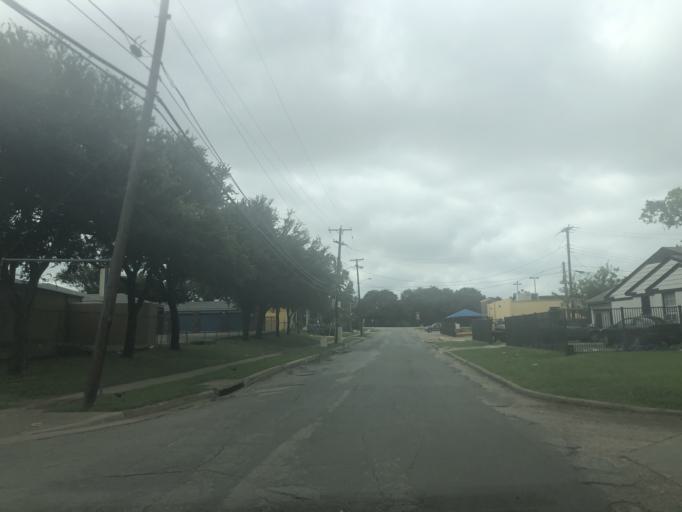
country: US
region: Texas
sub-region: Dallas County
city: University Park
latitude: 32.8572
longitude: -96.8658
